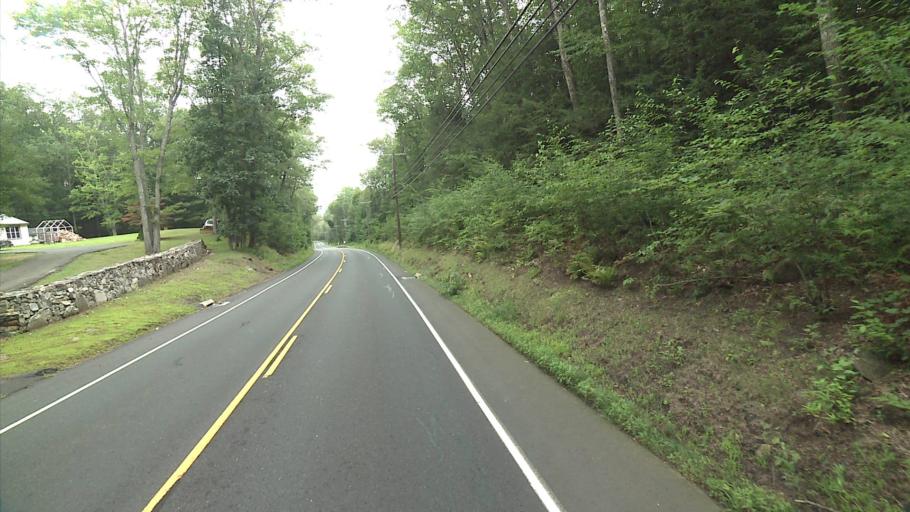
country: US
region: Connecticut
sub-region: Tolland County
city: Tolland
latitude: 41.8861
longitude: -72.3269
